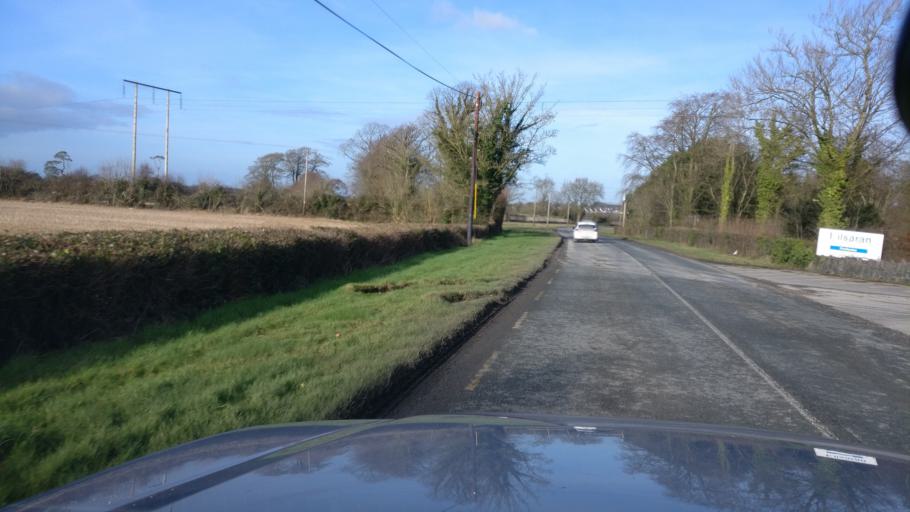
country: IE
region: Leinster
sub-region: Laois
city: Portlaoise
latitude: 53.0189
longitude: -7.2736
